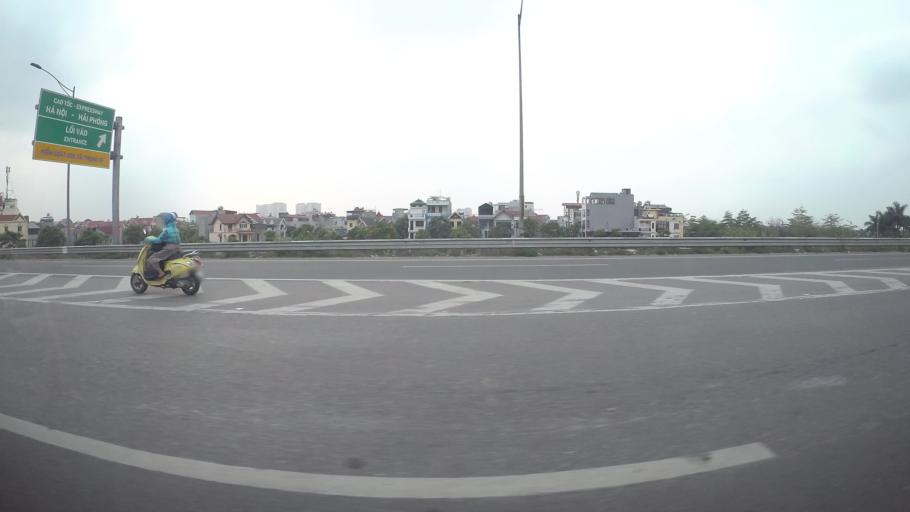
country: VN
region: Ha Noi
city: Trau Quy
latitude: 21.0158
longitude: 105.9205
